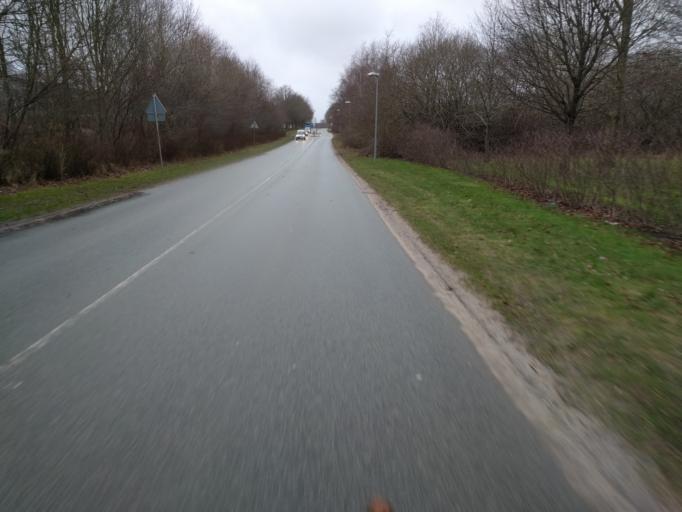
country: DK
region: Central Jutland
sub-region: Viborg Kommune
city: Viborg
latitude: 56.4644
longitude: 9.4544
